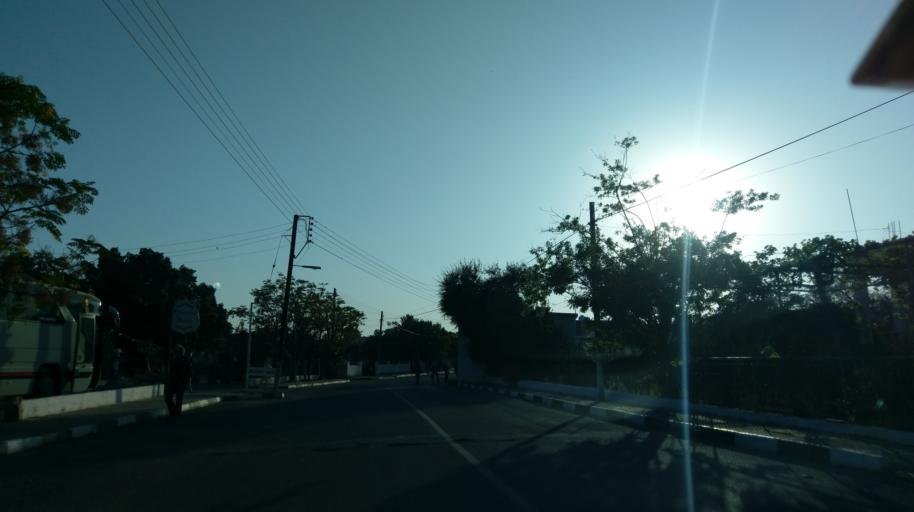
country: CY
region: Ammochostos
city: Leonarisso
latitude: 35.4125
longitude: 33.9994
